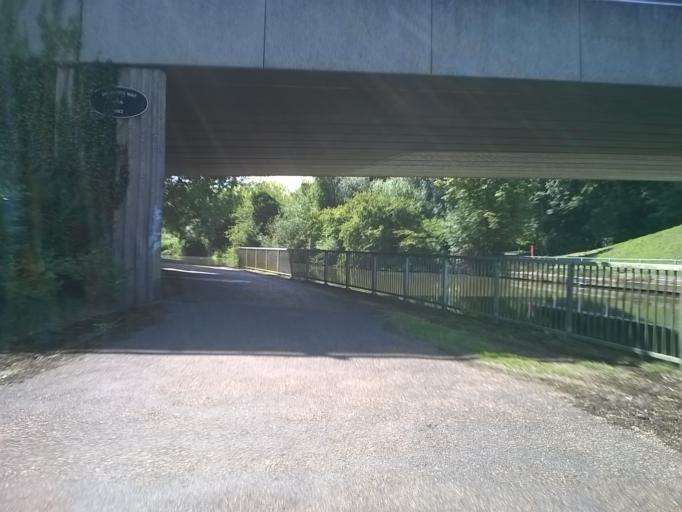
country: GB
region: England
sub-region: Milton Keynes
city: Milton Keynes
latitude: 52.0368
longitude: -0.7322
